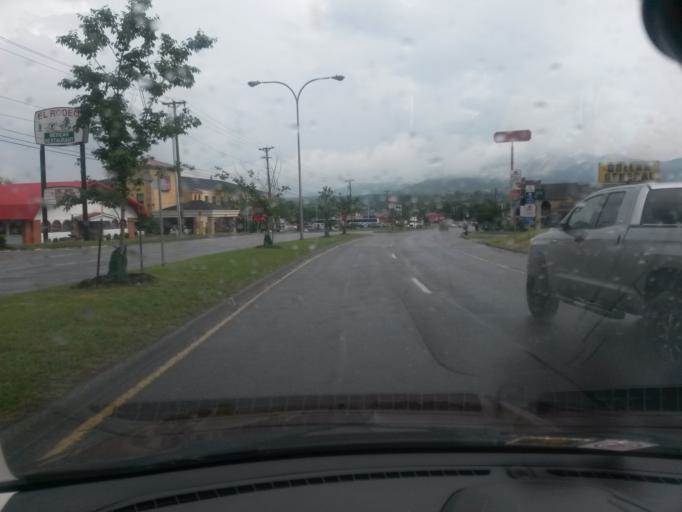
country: US
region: Virginia
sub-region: City of Salem
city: Salem
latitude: 37.2907
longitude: -80.0960
